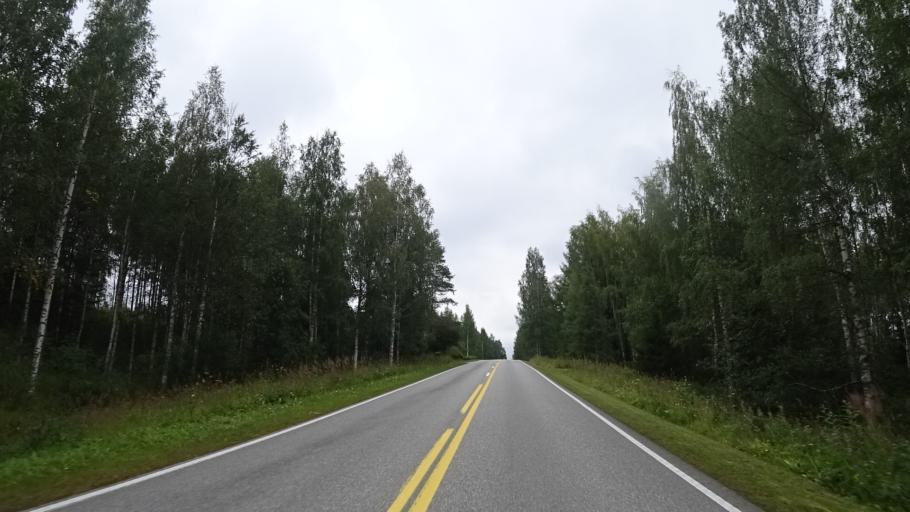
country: FI
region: North Karelia
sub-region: Pielisen Karjala
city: Lieksa
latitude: 63.2803
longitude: 30.5997
